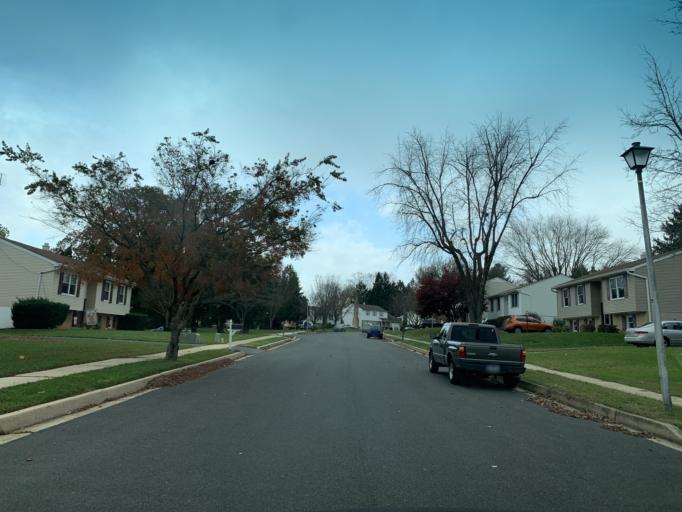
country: US
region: Maryland
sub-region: Harford County
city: Bel Air
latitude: 39.5432
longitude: -76.3446
